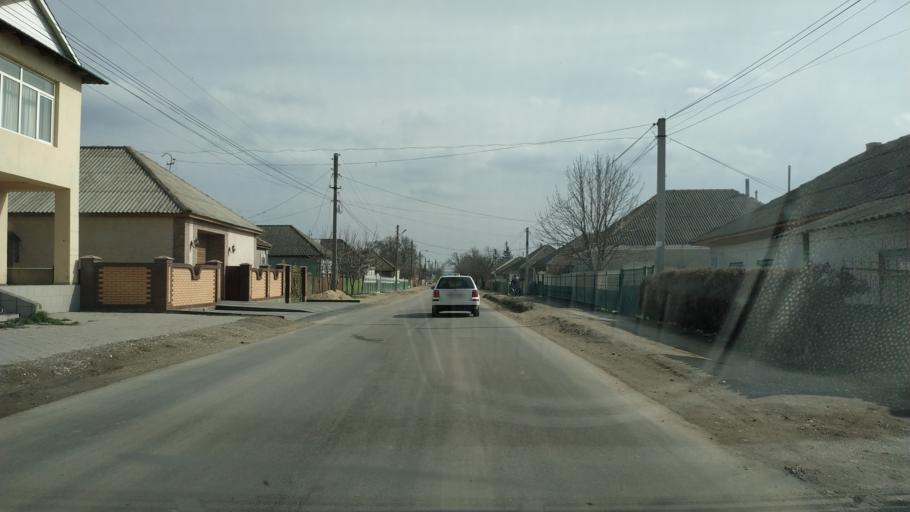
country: MD
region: Gagauzia
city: Vulcanesti
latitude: 45.6766
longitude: 28.4148
